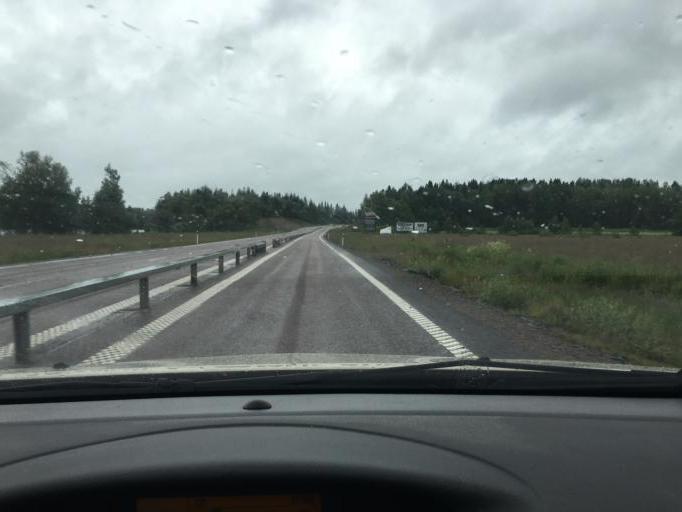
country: SE
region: Norrbotten
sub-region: Kalix Kommun
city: Rolfs
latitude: 65.8638
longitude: 23.0820
